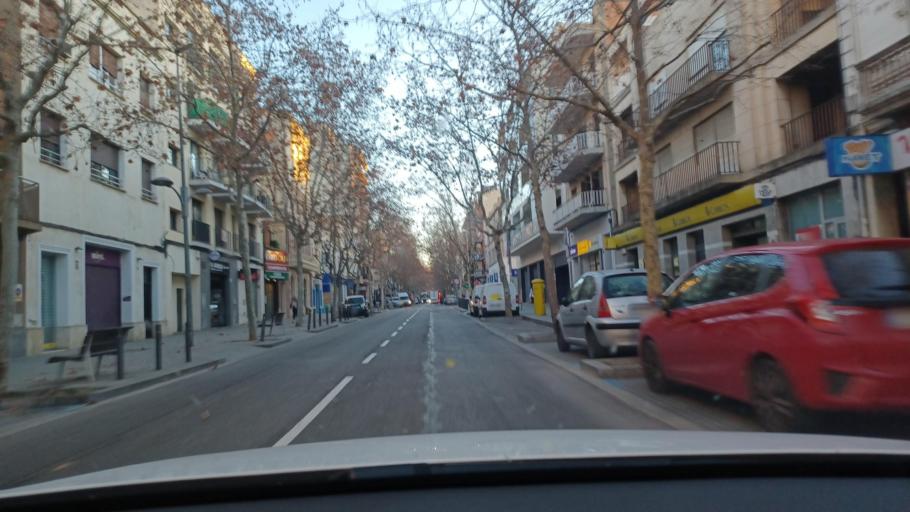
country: ES
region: Catalonia
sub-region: Provincia de Barcelona
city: Vilafranca del Penedes
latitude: 41.3420
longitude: 1.6952
